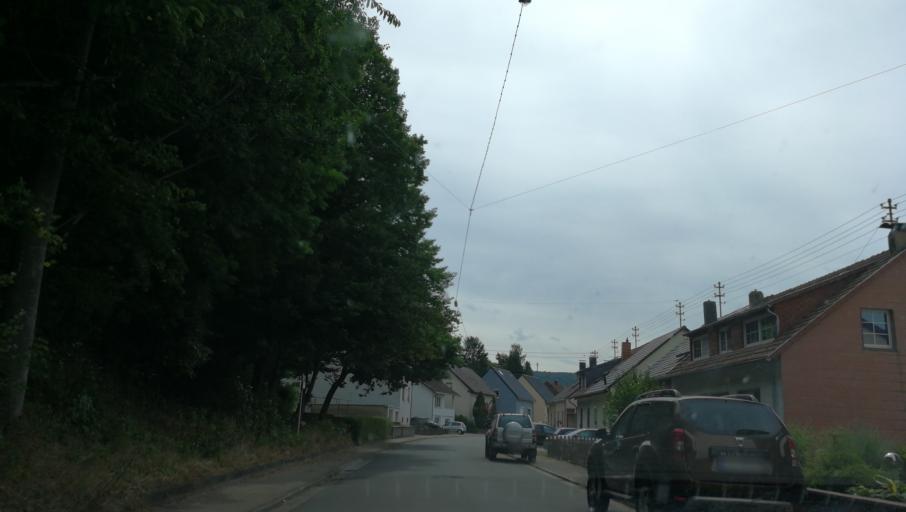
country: DE
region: Saarland
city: Britten
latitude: 49.4784
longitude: 6.6679
